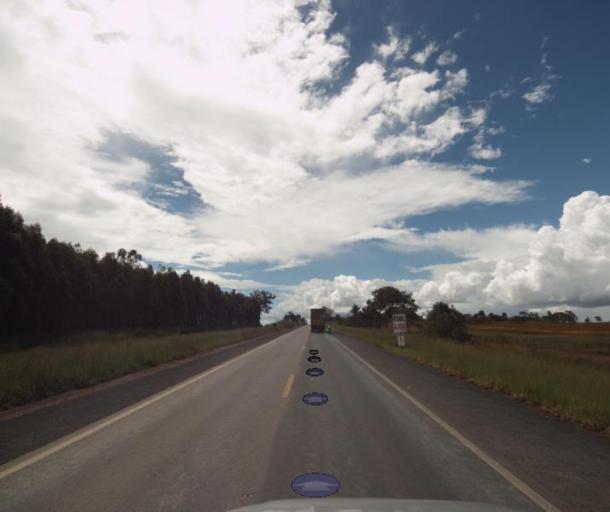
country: BR
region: Goias
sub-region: Uruacu
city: Uruacu
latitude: -14.1689
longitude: -49.1242
